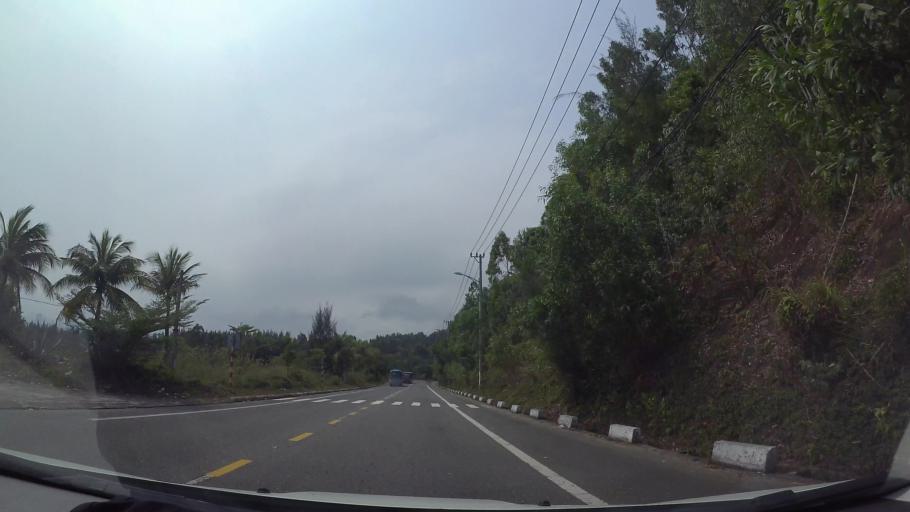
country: VN
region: Da Nang
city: Son Tra
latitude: 16.1001
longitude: 108.2726
